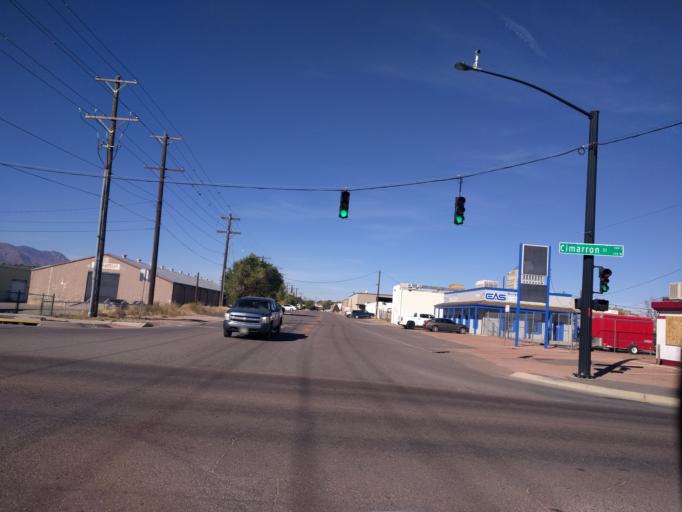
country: US
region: Colorado
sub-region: El Paso County
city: Colorado Springs
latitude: 38.8270
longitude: -104.8293
